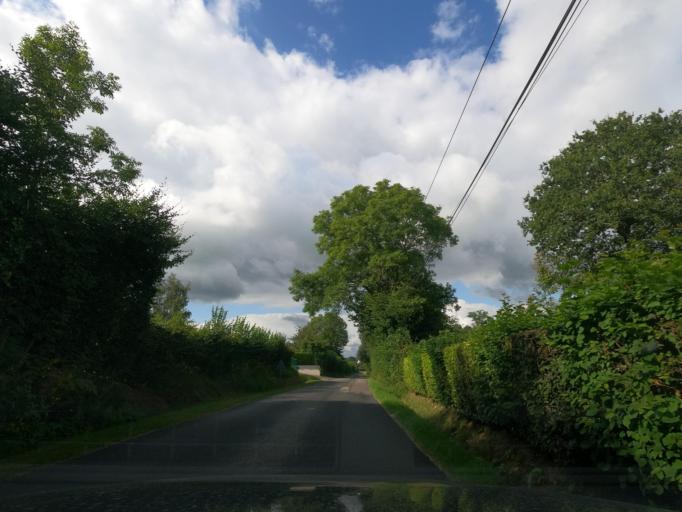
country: FR
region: Lower Normandy
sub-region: Departement de l'Orne
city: Gace
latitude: 48.7853
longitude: 0.2600
